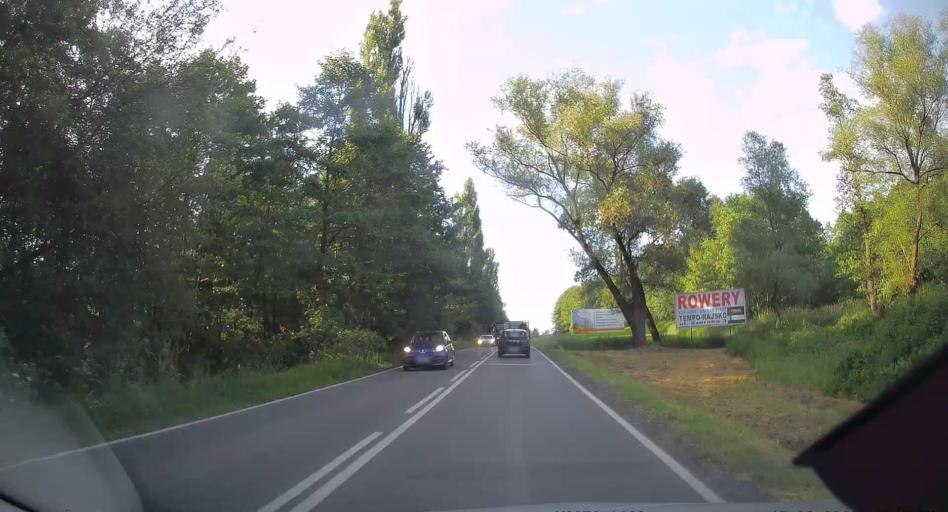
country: PL
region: Lesser Poland Voivodeship
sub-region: Powiat oswiecimski
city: Grojec
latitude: 49.9744
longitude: 19.2215
